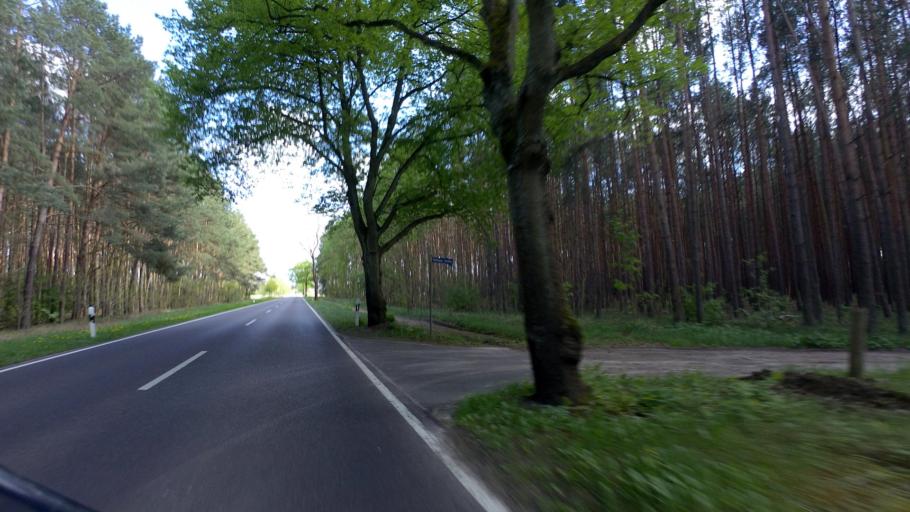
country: DE
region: Brandenburg
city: Zehdenick
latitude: 52.9569
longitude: 13.3756
